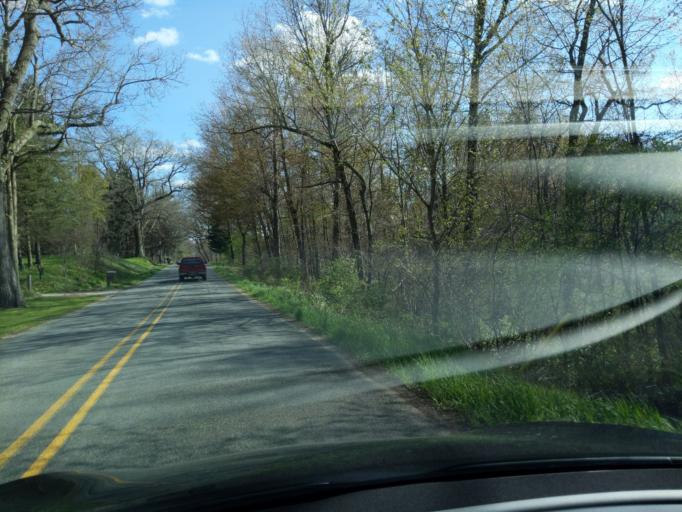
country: US
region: Michigan
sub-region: Jackson County
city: Spring Arbor
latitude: 42.3275
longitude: -84.5214
